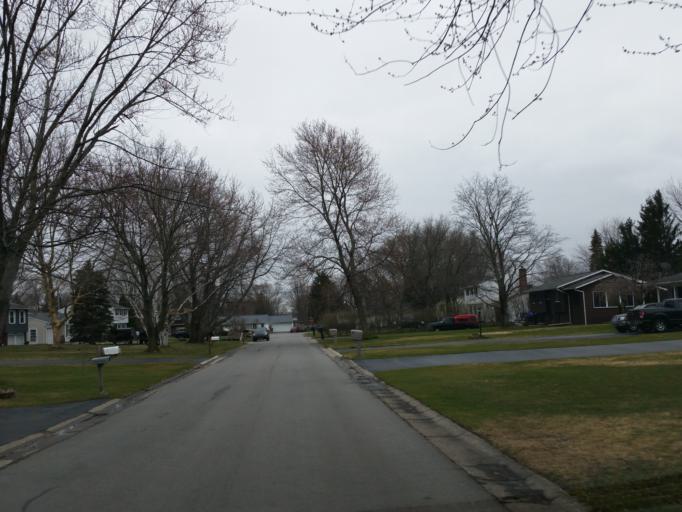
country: US
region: New York
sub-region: Monroe County
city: Scottsville
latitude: 43.1086
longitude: -77.7591
